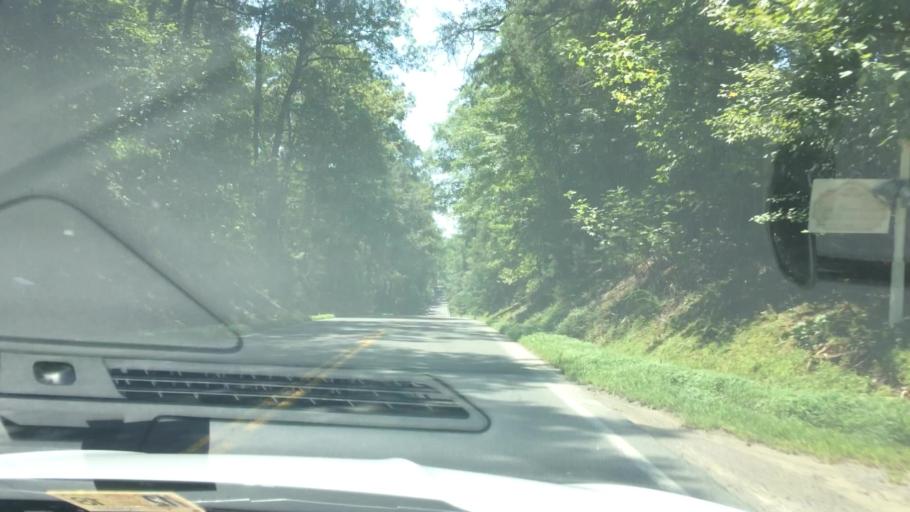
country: US
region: Virginia
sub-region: Charles City County
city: Charles City
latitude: 37.4030
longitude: -77.0474
